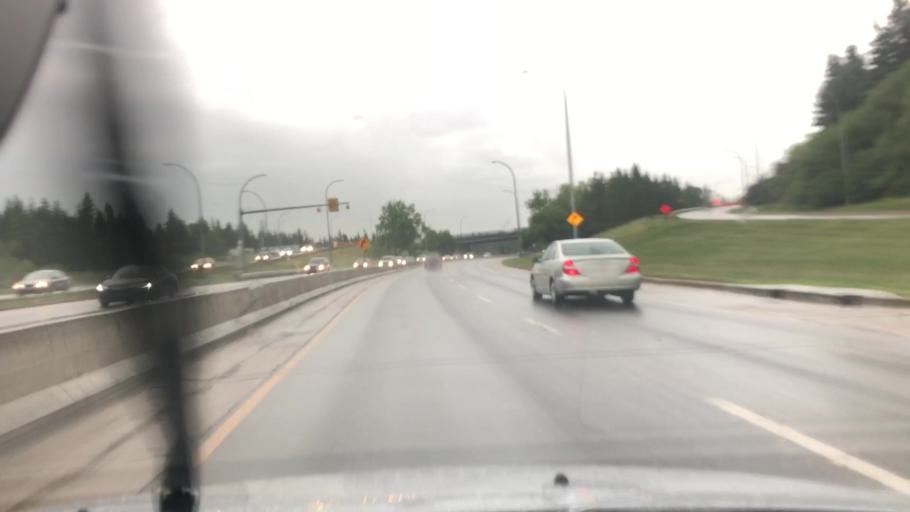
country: CA
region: Alberta
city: Edmonton
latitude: 53.5519
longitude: -113.4378
